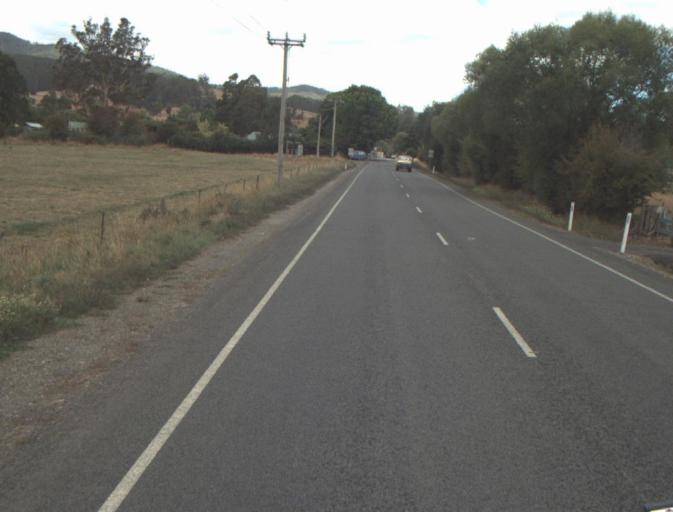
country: AU
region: Tasmania
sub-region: Launceston
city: Mayfield
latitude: -41.2464
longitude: 147.2174
